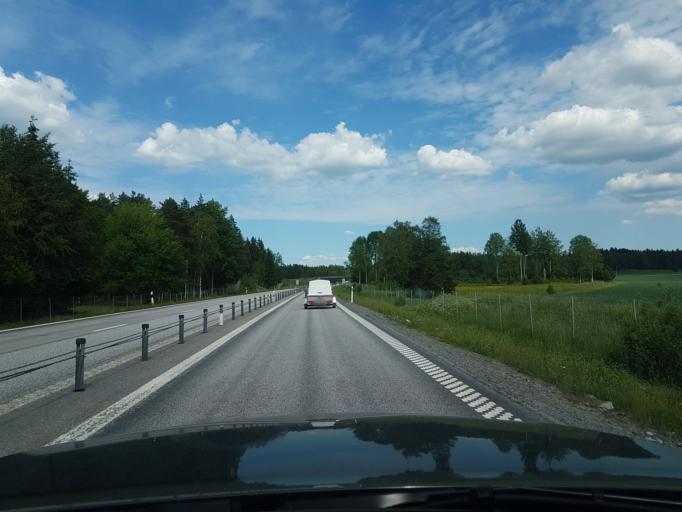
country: SE
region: Stockholm
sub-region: Osterakers Kommun
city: Akersberga
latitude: 59.6061
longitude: 18.2783
